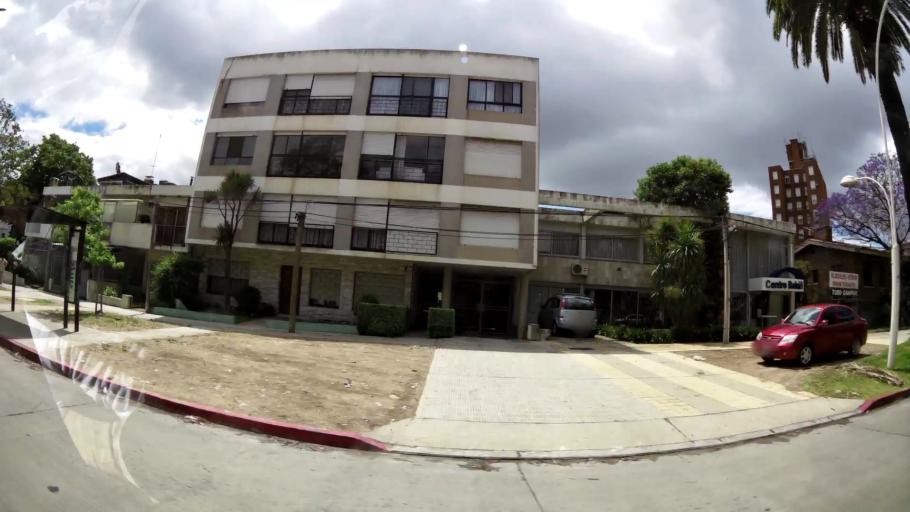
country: UY
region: Montevideo
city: Montevideo
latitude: -34.8820
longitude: -56.1663
